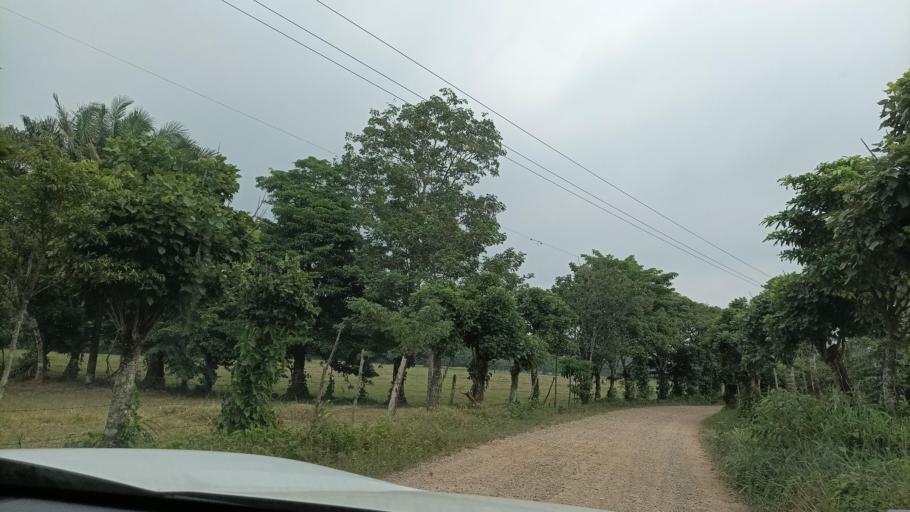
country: MX
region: Veracruz
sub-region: Uxpanapa
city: Poblado 10
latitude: 17.5478
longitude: -94.2317
